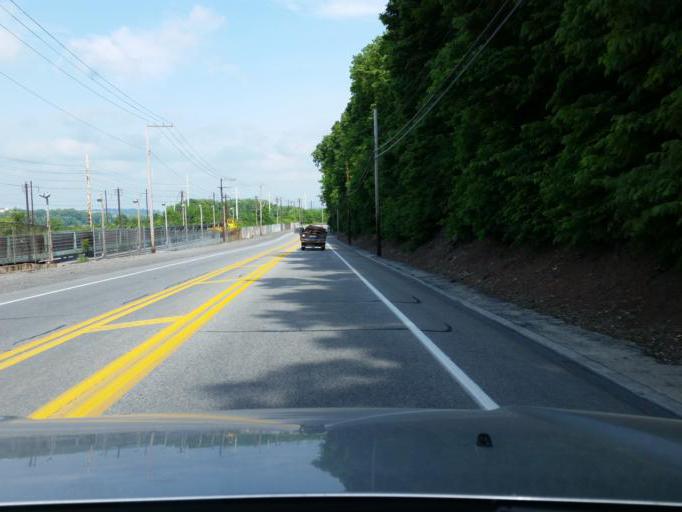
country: US
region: Pennsylvania
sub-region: Dauphin County
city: Bressler
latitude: 40.2163
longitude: -76.8146
